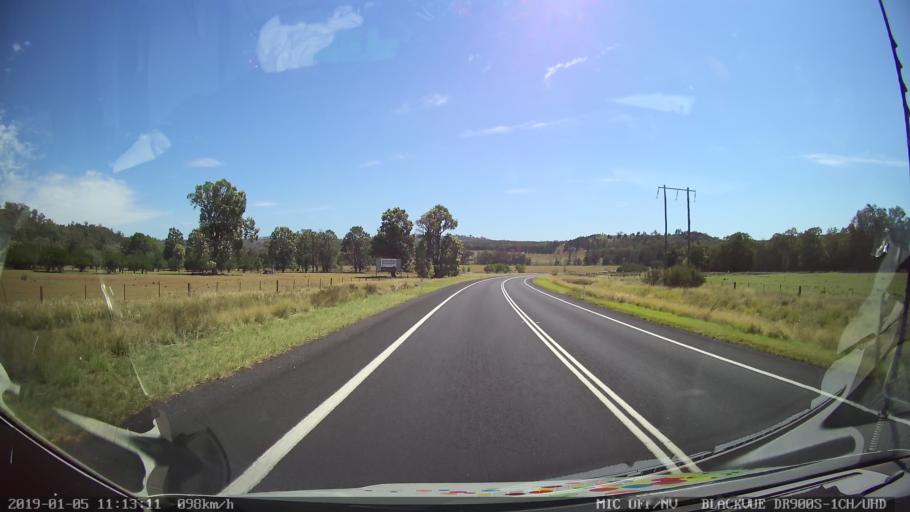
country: AU
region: New South Wales
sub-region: Warrumbungle Shire
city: Coonabarabran
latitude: -31.3733
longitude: 149.2678
